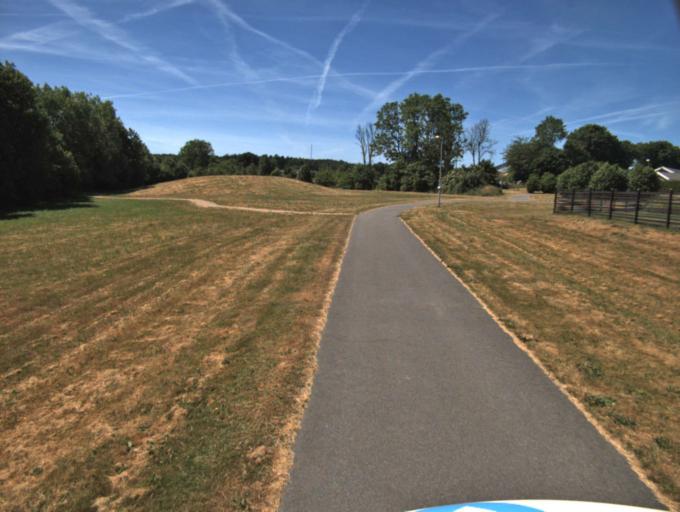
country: SE
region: Skane
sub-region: Kristianstads Kommun
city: Onnestad
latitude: 56.0521
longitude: 14.0181
